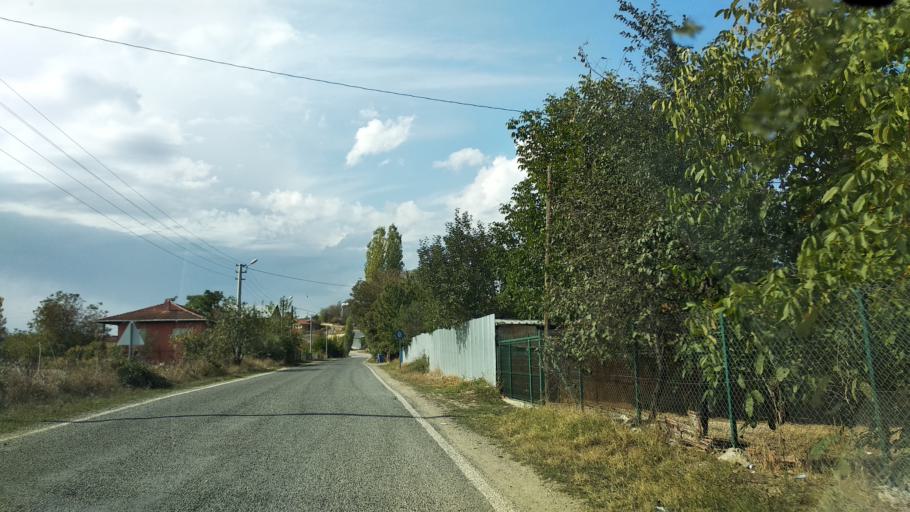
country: TR
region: Bolu
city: Seben
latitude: 40.4061
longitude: 31.5715
